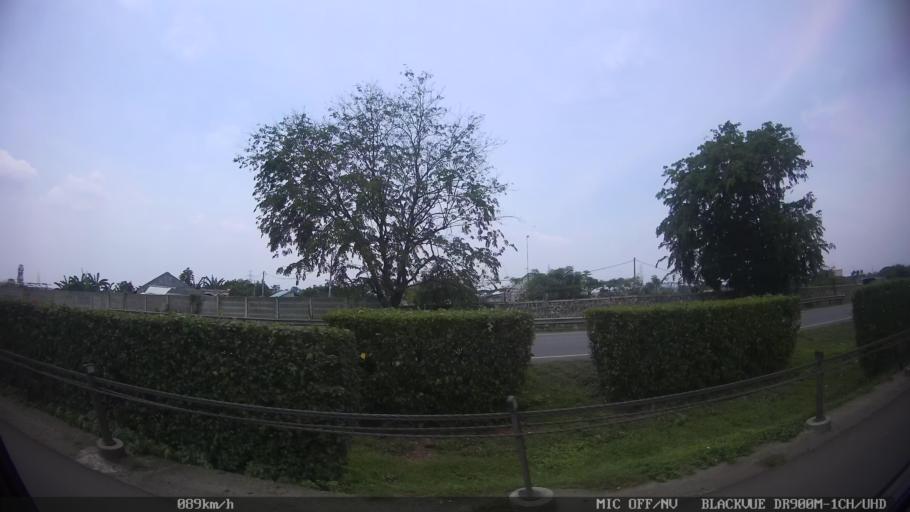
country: ID
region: West Java
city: Kresek
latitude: -6.1599
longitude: 106.3279
